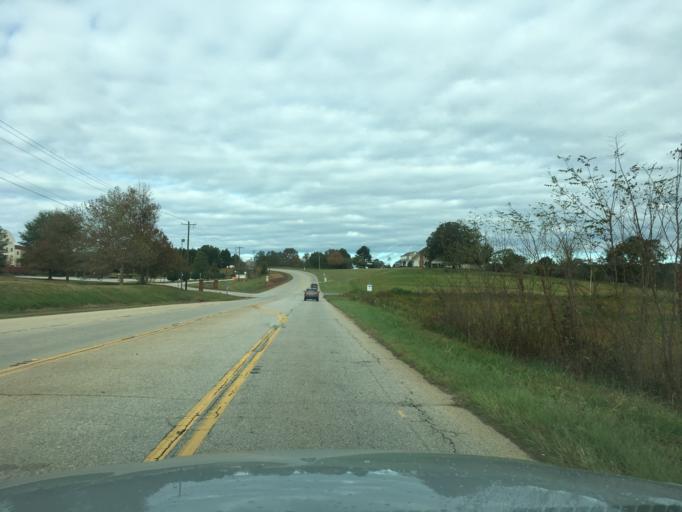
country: US
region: South Carolina
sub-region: Greenville County
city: Greer
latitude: 34.9817
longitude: -82.2288
